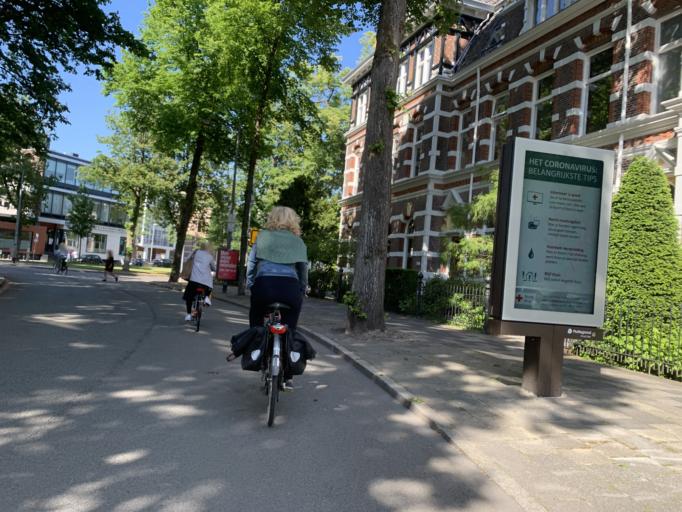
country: NL
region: Groningen
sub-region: Gemeente Groningen
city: Groningen
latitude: 53.2130
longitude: 6.5701
